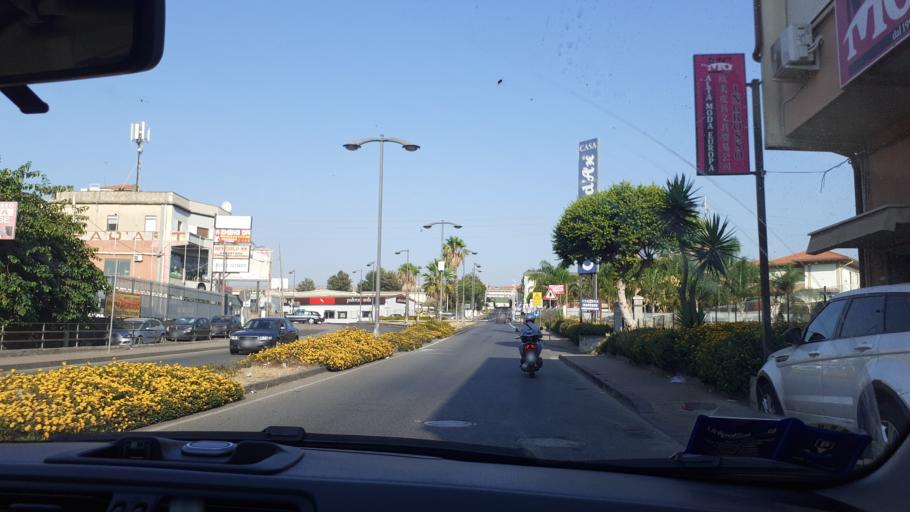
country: IT
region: Sicily
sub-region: Catania
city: Misterbianco
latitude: 37.5148
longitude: 15.0237
